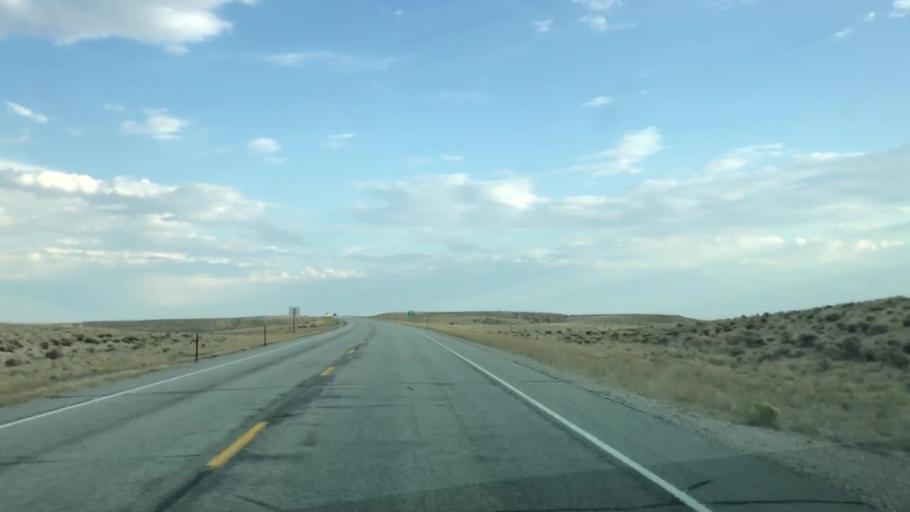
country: US
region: Wyoming
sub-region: Sweetwater County
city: North Rock Springs
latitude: 42.2814
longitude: -109.4860
